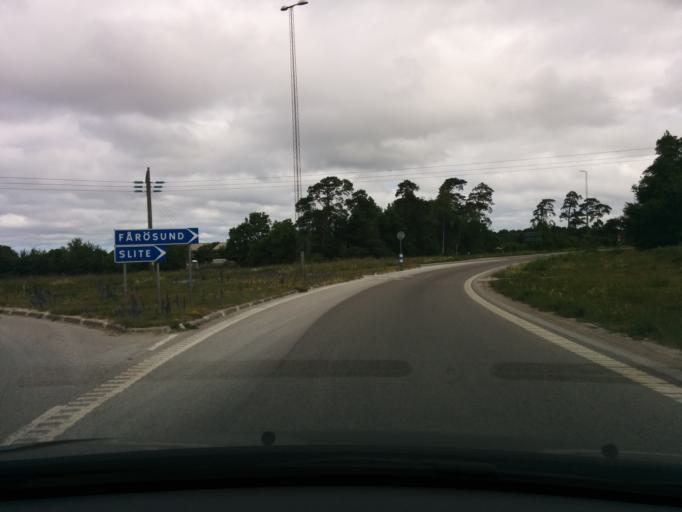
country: SE
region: Gotland
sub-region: Gotland
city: Visby
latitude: 57.6253
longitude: 18.3219
